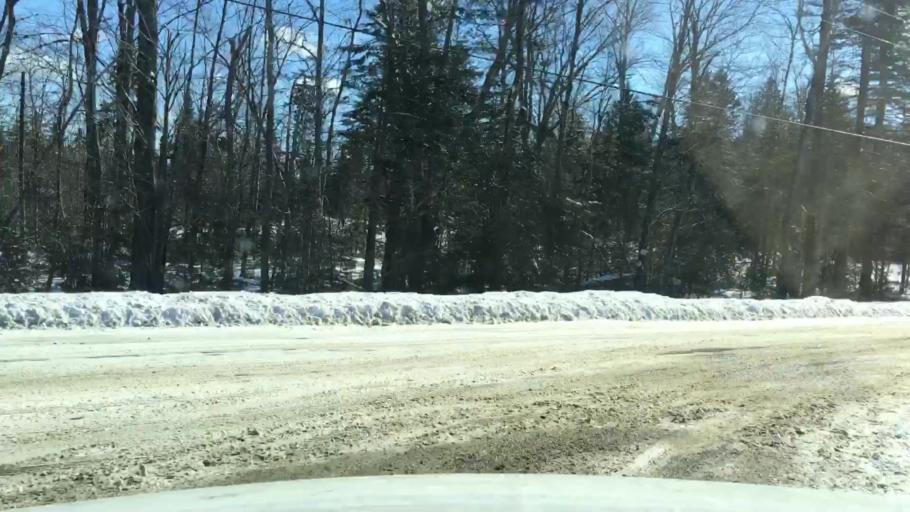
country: US
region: Maine
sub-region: Washington County
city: Calais
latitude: 45.0697
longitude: -67.4752
